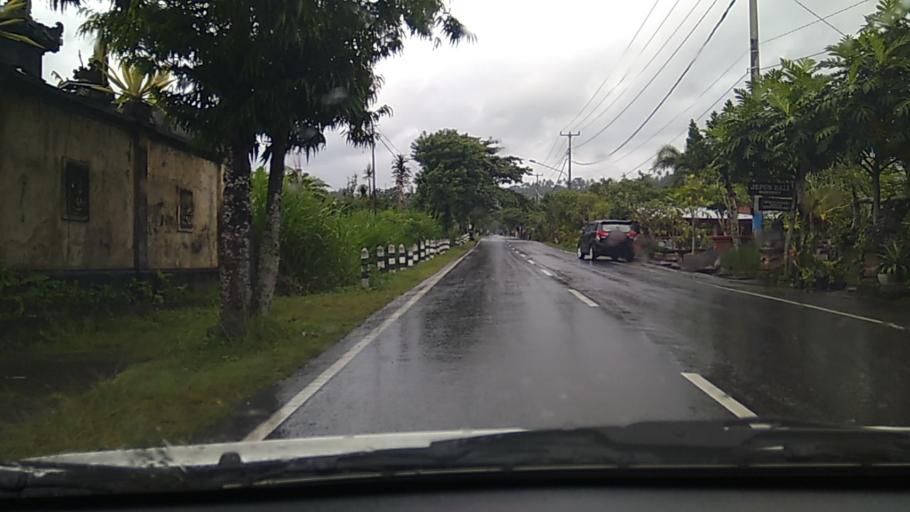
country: ID
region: Bali
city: Banjar Ababi
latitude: -8.4176
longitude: 115.5907
